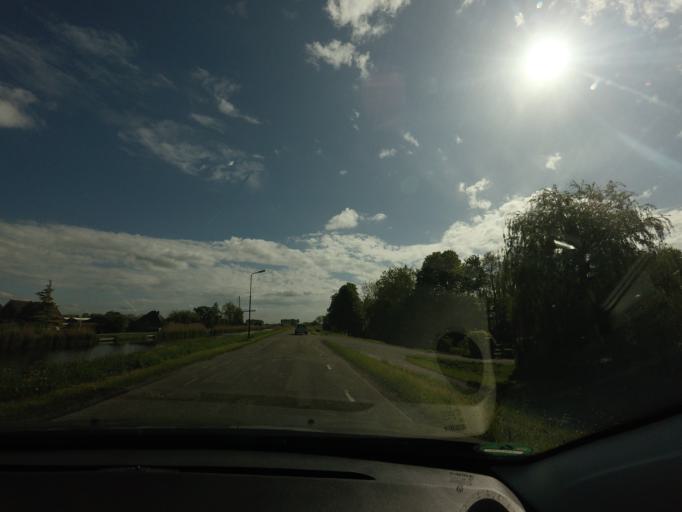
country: NL
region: North Holland
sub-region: Gemeente Heerhugowaard
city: Heerhugowaard
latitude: 52.6628
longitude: 4.8674
